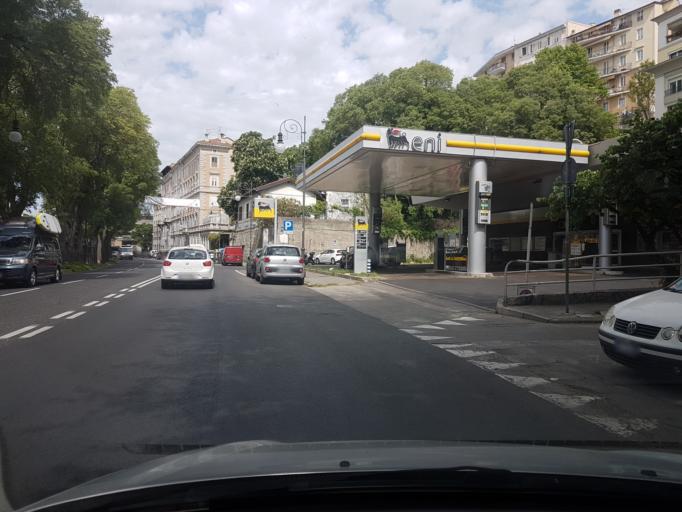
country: IT
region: Friuli Venezia Giulia
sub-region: Provincia di Trieste
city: Trieste
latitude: 45.6647
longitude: 13.7676
